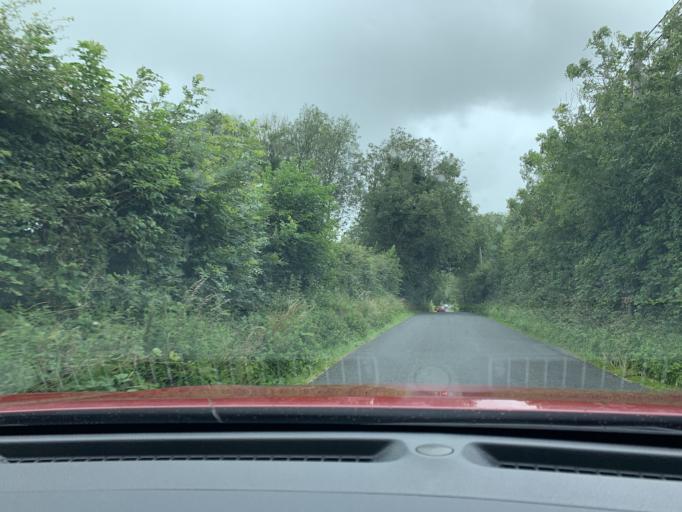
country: IE
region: Connaught
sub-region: County Leitrim
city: Carrick-on-Shannon
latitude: 53.8646
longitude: -8.1374
